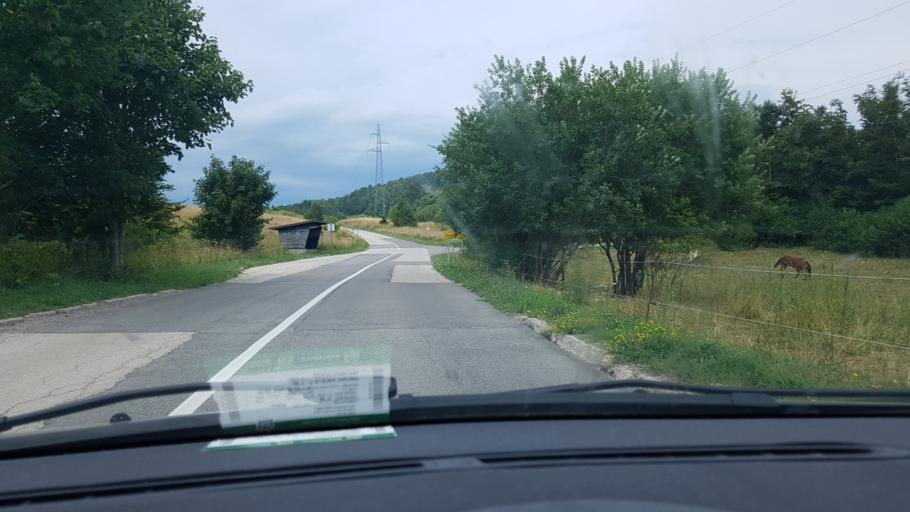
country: HR
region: Primorsko-Goranska
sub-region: Grad Delnice
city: Delnice
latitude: 45.3332
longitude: 14.7469
